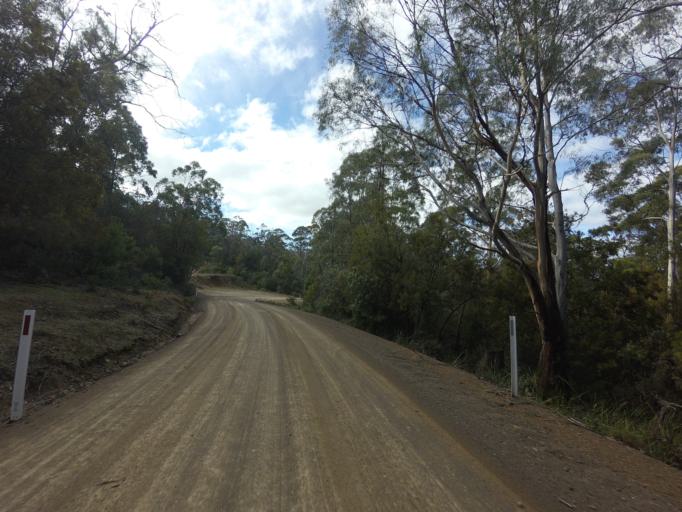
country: AU
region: Tasmania
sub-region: Clarence
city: Sandford
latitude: -43.0876
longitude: 147.7072
